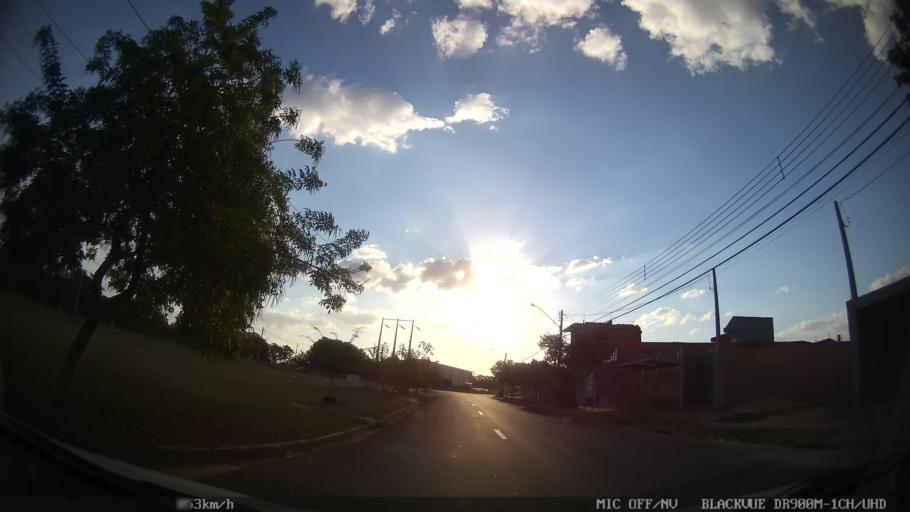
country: BR
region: Sao Paulo
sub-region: Ribeirao Preto
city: Ribeirao Preto
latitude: -21.1940
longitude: -47.7367
